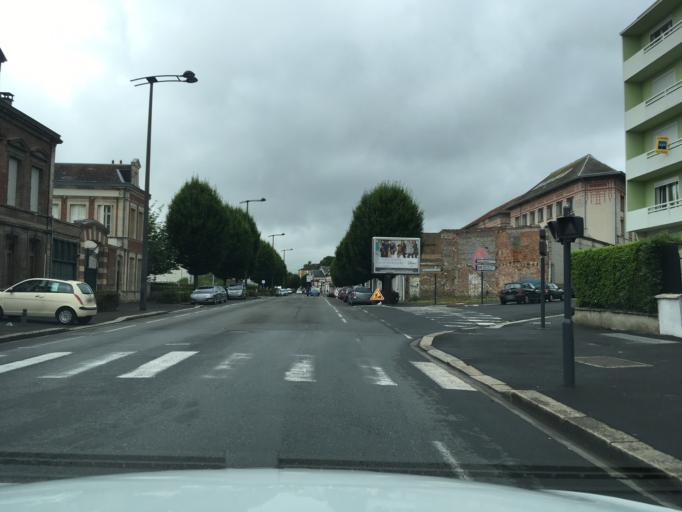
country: FR
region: Picardie
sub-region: Departement de l'Aisne
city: Saint-Quentin
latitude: 49.8413
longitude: 3.2860
